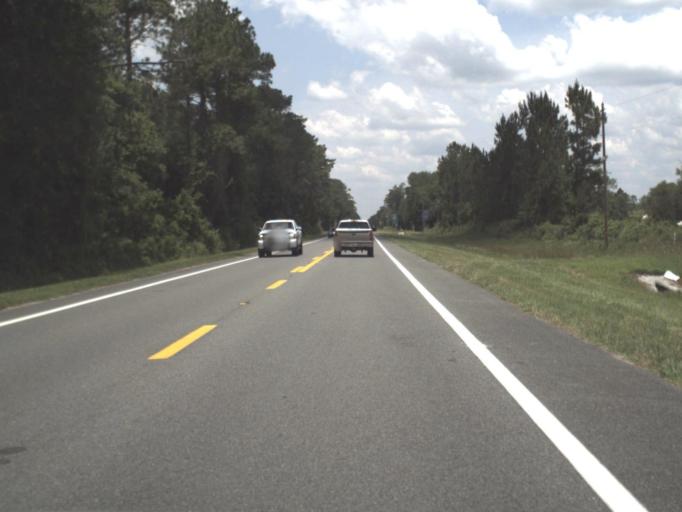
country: US
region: Florida
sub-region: Union County
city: Lake Butler
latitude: 30.0880
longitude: -82.4629
